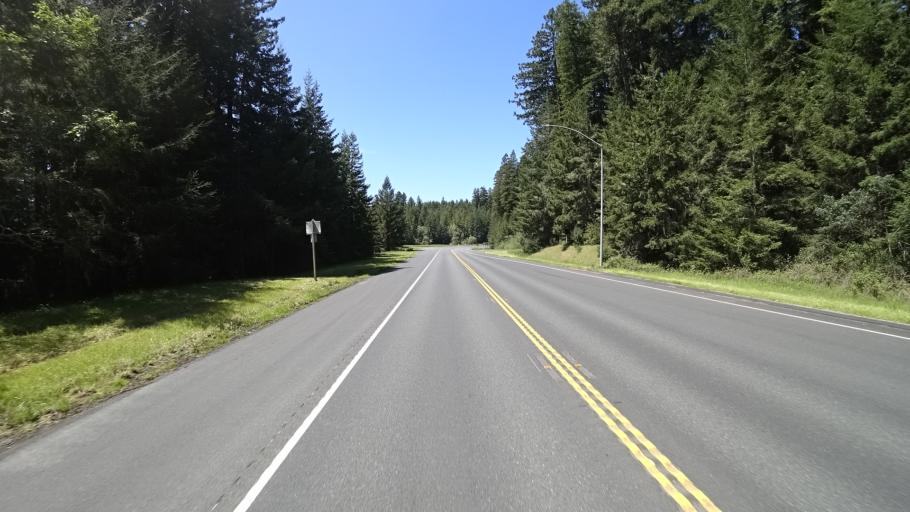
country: US
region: California
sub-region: Humboldt County
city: Blue Lake
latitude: 40.8841
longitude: -123.9659
